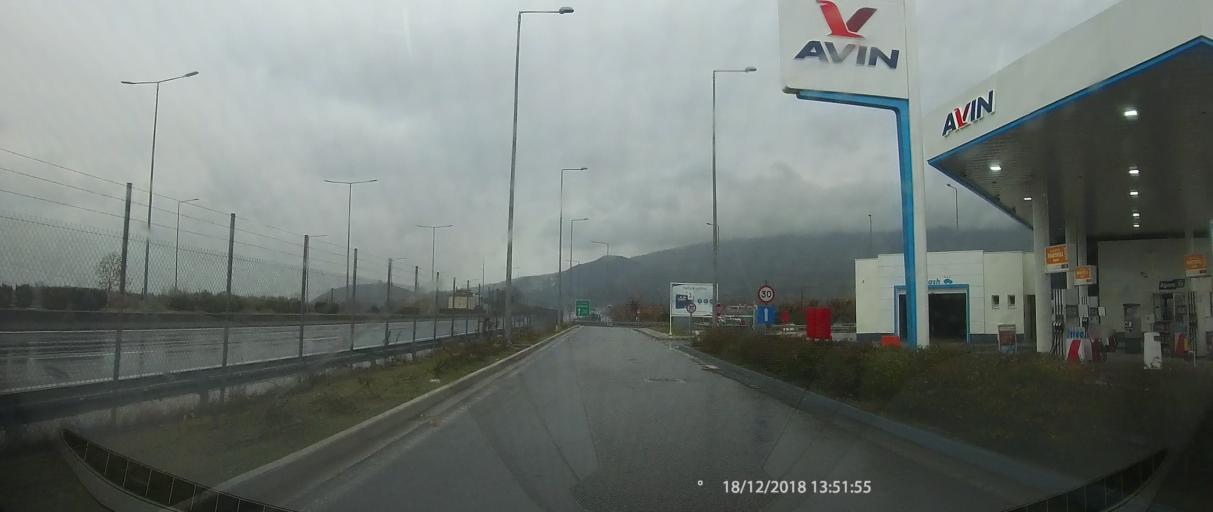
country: GR
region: Central Macedonia
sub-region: Nomos Pierias
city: Leptokarya
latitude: 40.0267
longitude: 22.5732
